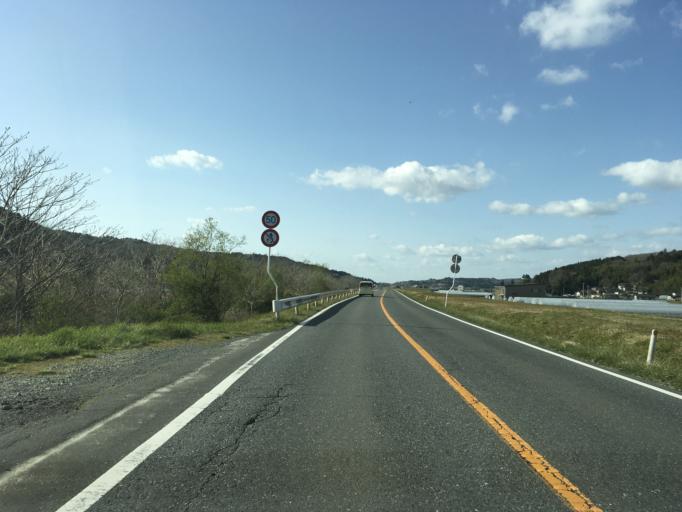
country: JP
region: Miyagi
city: Wakuya
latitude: 38.6280
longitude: 141.2930
